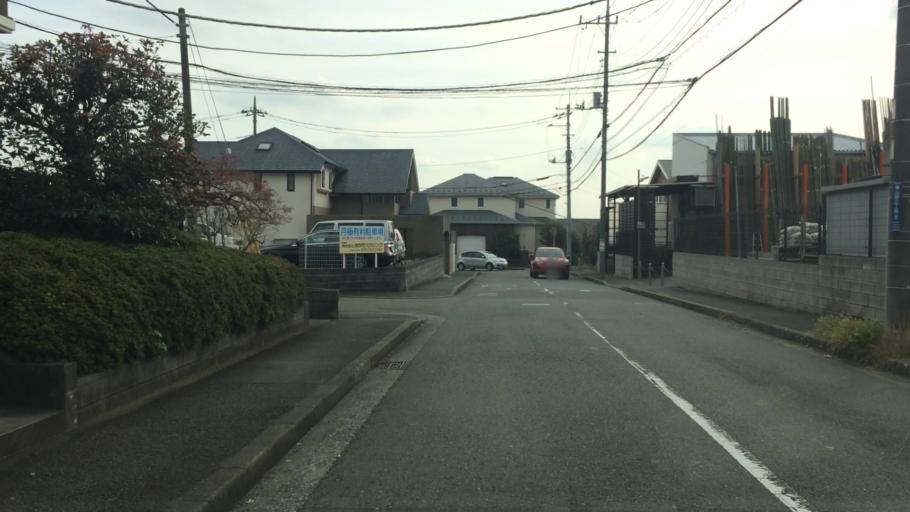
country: JP
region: Tokyo
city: Chofugaoka
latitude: 35.5607
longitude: 139.6004
